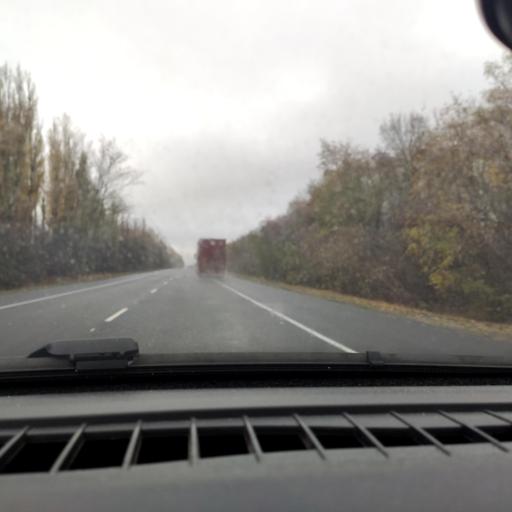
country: RU
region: Voronezj
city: Kolodeznyy
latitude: 51.2469
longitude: 39.0555
